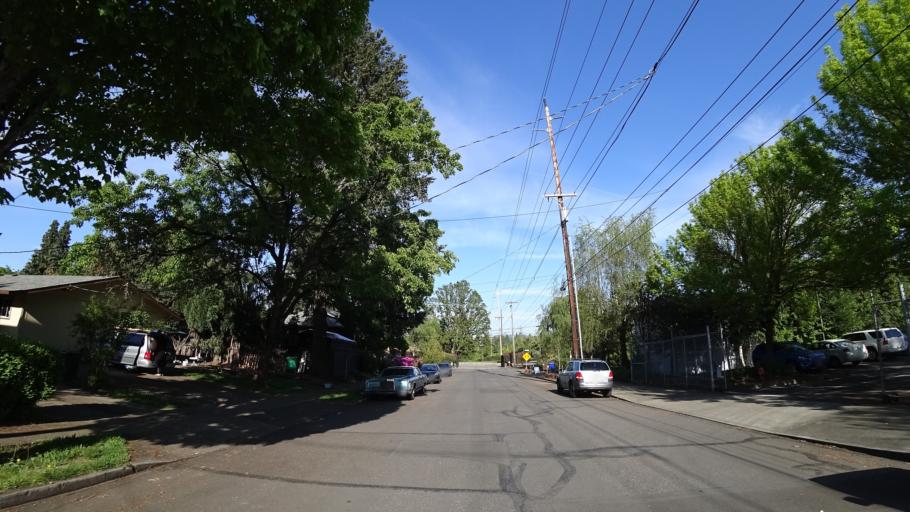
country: US
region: Oregon
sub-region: Clackamas County
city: Milwaukie
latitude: 45.4593
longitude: -122.6458
